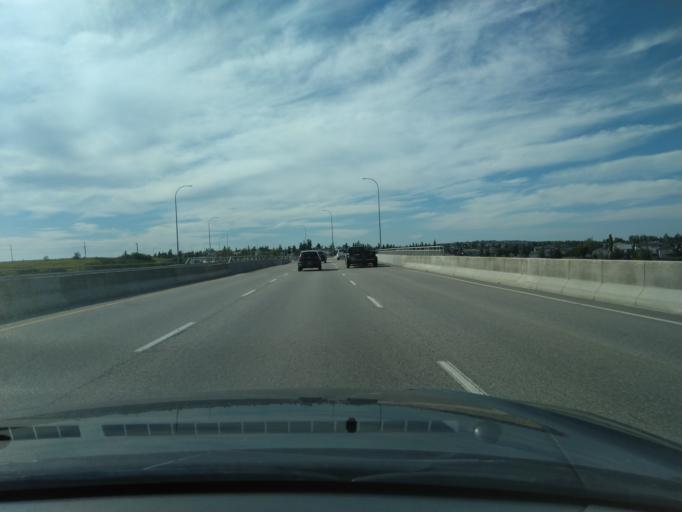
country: CA
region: Alberta
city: Calgary
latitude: 51.1424
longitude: -114.0420
